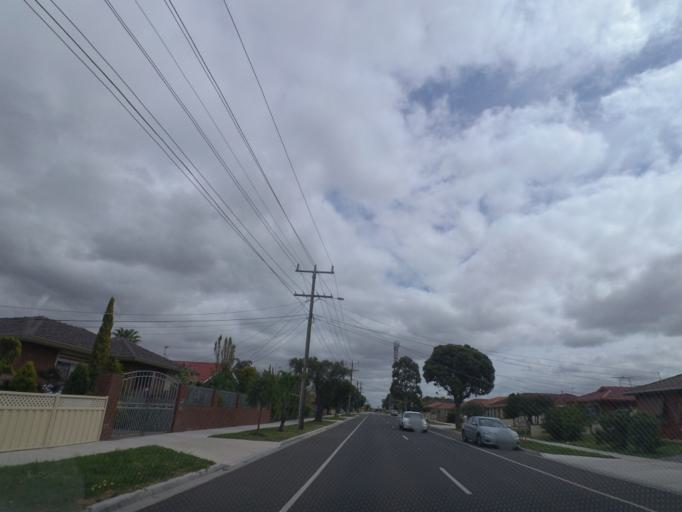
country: AU
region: Victoria
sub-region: Brimbank
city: Deer Park
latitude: -37.7587
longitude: 144.7642
